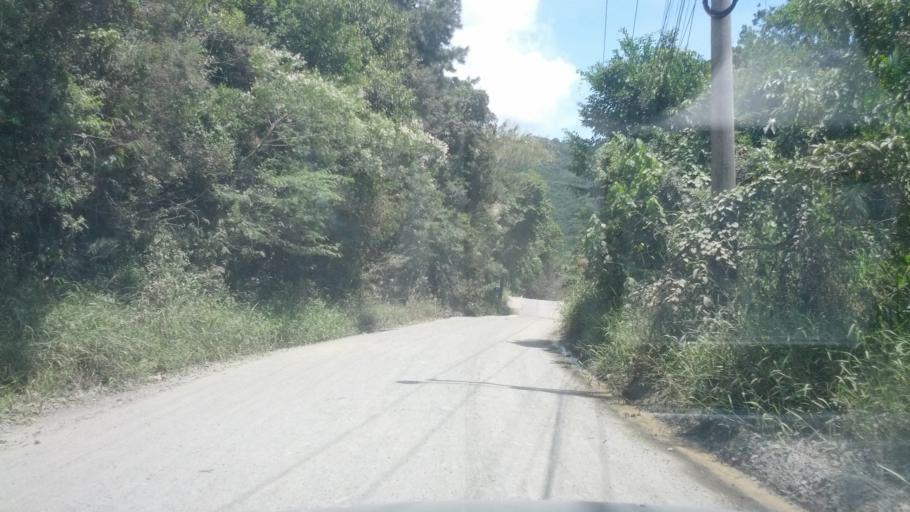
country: BR
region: Santa Catarina
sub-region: Porto Belo
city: Porto Belo
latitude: -27.1599
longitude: -48.5376
